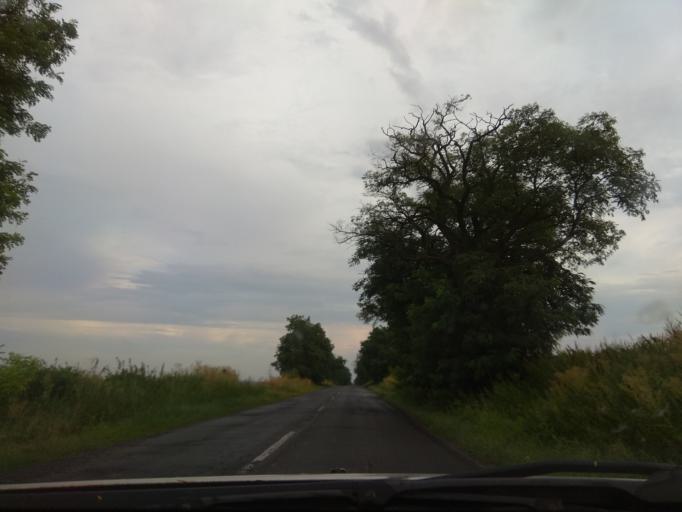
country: HU
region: Borsod-Abauj-Zemplen
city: Gesztely
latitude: 48.1340
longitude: 20.9735
